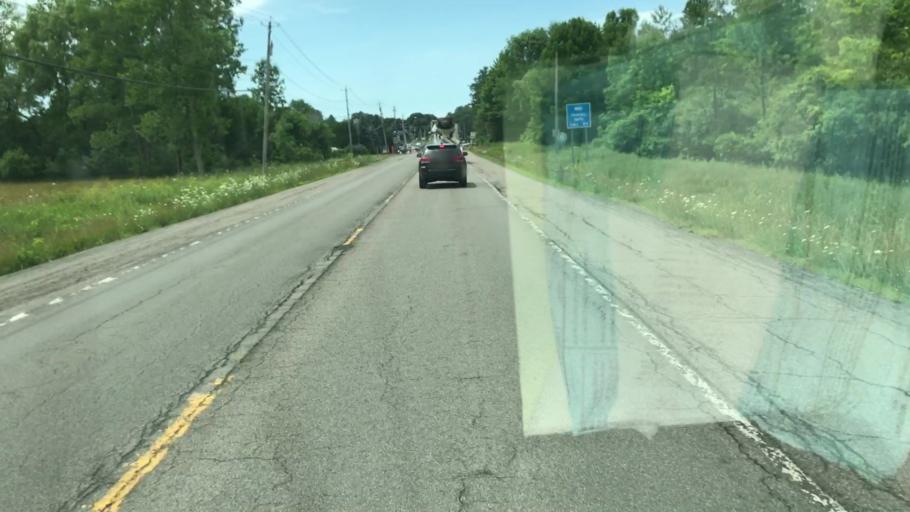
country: US
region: New York
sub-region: Onondaga County
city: Skaneateles
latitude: 42.9449
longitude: -76.4052
